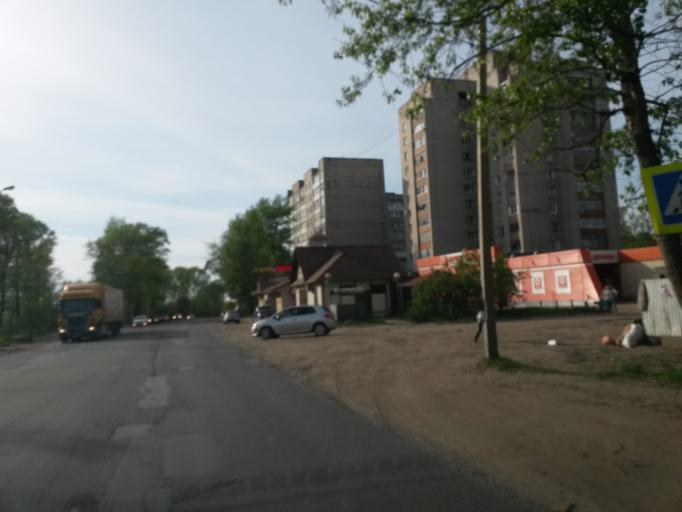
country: RU
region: Jaroslavl
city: Yaroslavl
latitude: 57.5829
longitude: 39.8261
